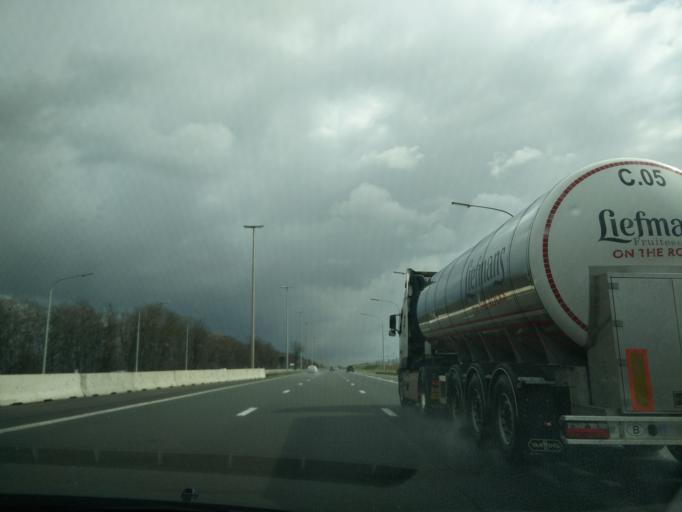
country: BE
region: Wallonia
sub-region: Province de Liege
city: Remicourt
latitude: 50.7042
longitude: 5.2989
